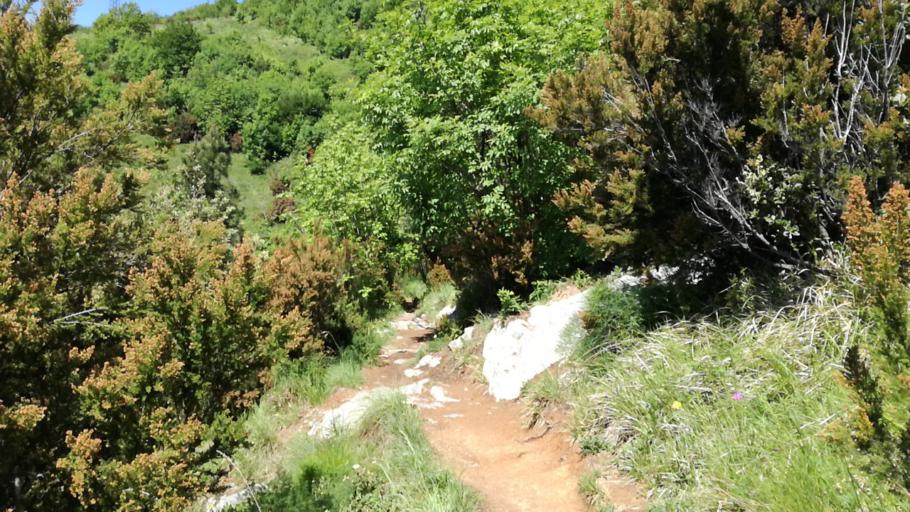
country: IT
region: Liguria
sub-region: Provincia di Genova
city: Genoa
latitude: 44.4330
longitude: 8.9182
